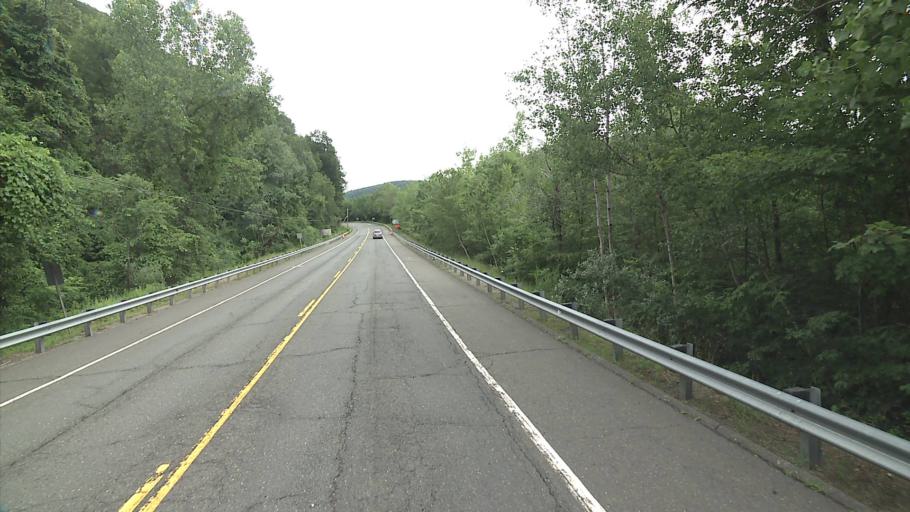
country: US
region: Connecticut
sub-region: Litchfield County
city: Winsted
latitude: 42.0388
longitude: -73.0561
